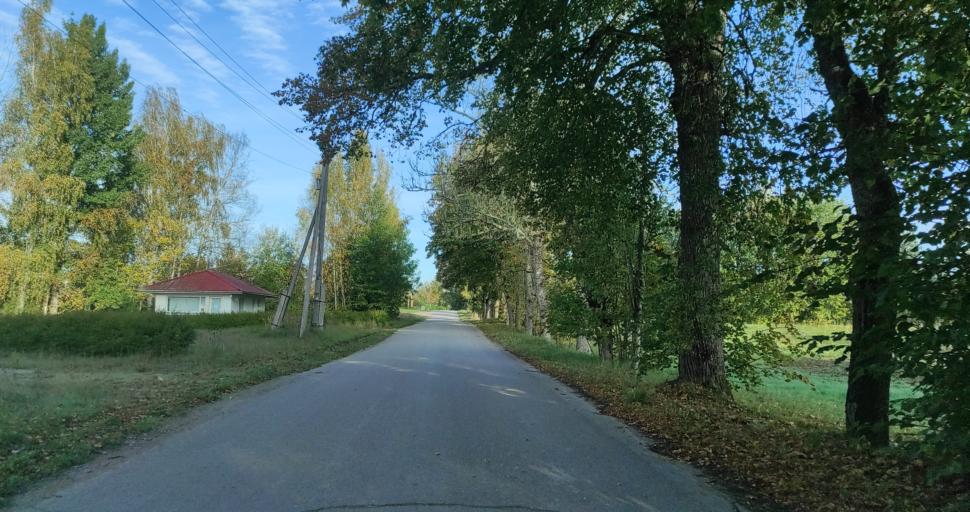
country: LV
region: Skrunda
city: Skrunda
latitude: 56.7415
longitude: 21.8810
